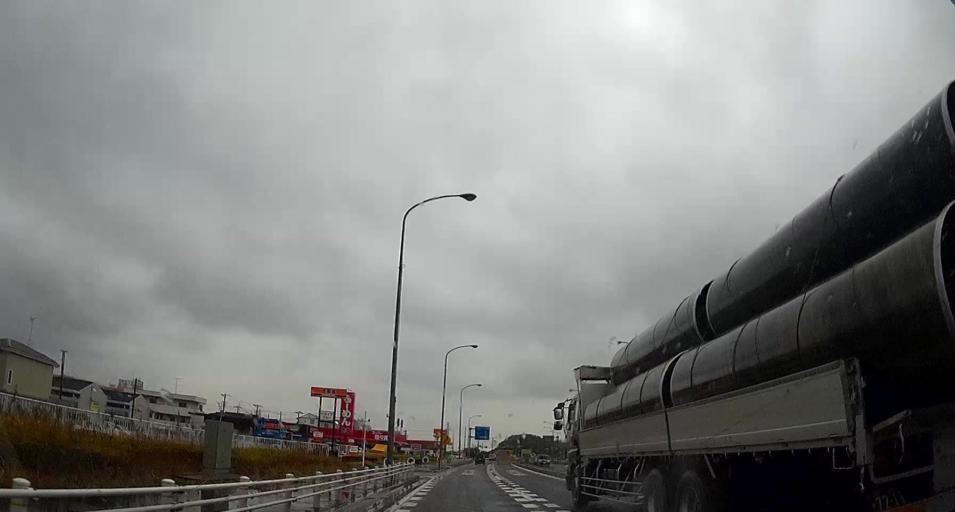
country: JP
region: Chiba
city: Ichihara
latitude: 35.5294
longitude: 140.1010
